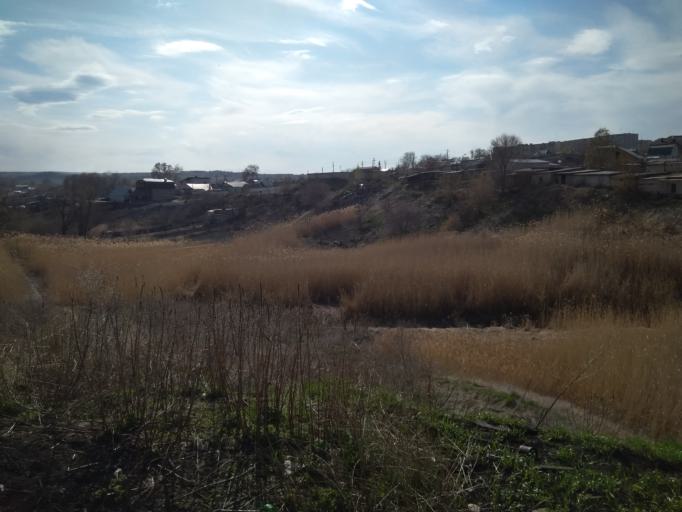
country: RU
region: Ulyanovsk
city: Novoul'yanovsk
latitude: 54.1470
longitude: 48.3972
